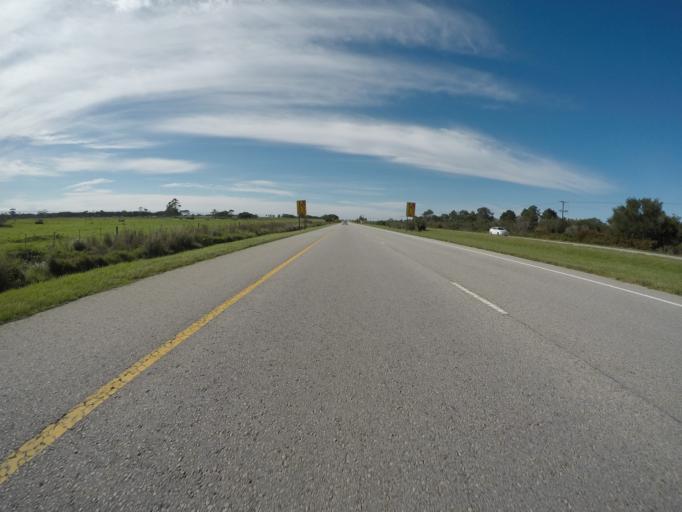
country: ZA
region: Eastern Cape
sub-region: Nelson Mandela Bay Metropolitan Municipality
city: Uitenhage
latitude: -33.9161
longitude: 25.2808
